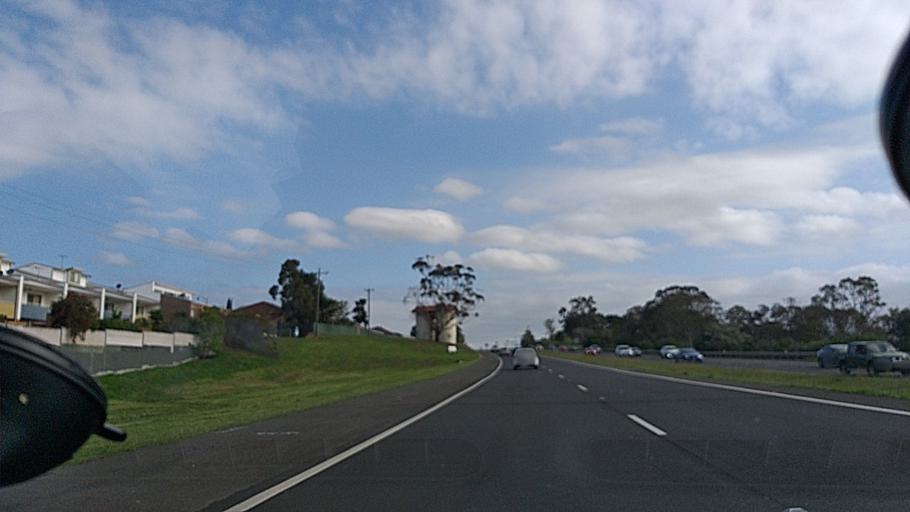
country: AU
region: New South Wales
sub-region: Campbelltown Municipality
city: Campbelltown
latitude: -34.0848
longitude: 150.8070
